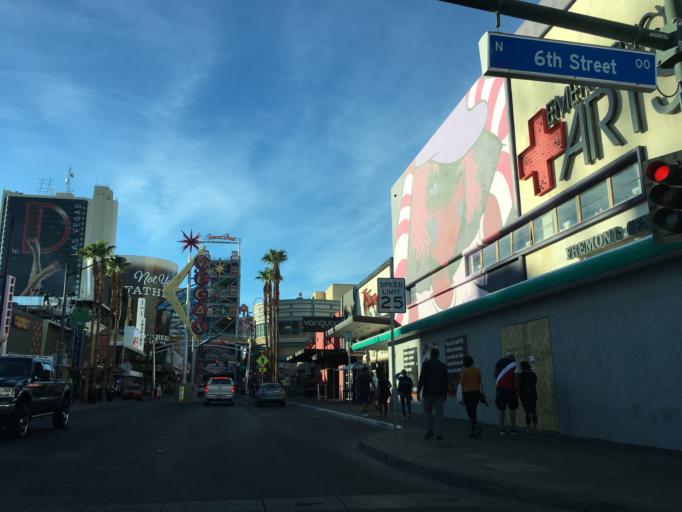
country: US
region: Nevada
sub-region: Clark County
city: Las Vegas
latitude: 36.1688
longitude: -115.1396
